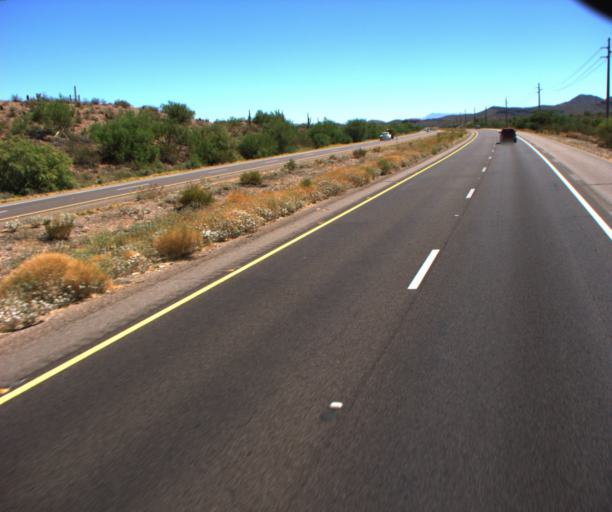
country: US
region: Arizona
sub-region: Maricopa County
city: Fountain Hills
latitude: 33.5204
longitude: -111.7427
